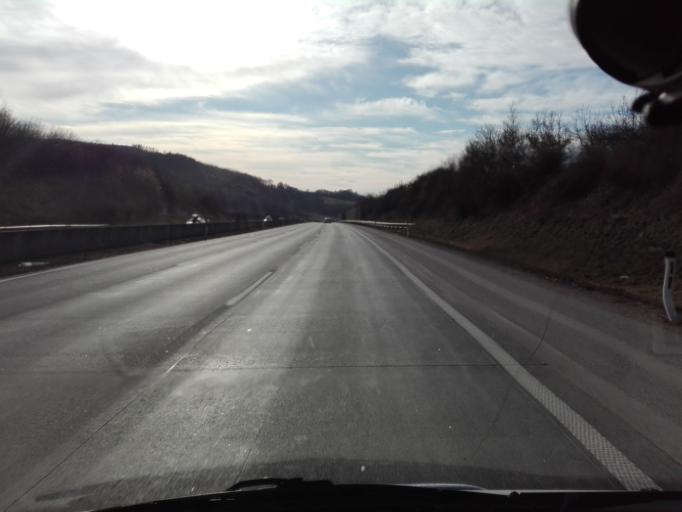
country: AT
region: Lower Austria
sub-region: Politischer Bezirk Melk
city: Melk
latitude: 48.2175
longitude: 15.3203
